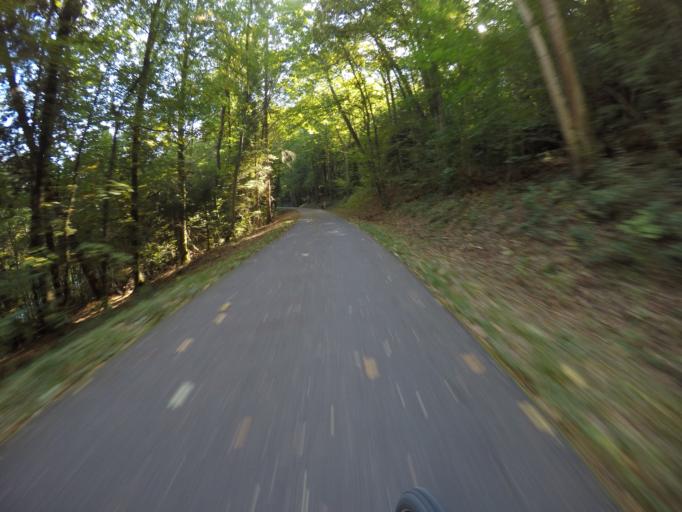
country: DE
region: Baden-Wuerttemberg
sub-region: Regierungsbezirk Stuttgart
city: Steinenbronn
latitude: 48.6805
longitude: 9.1251
